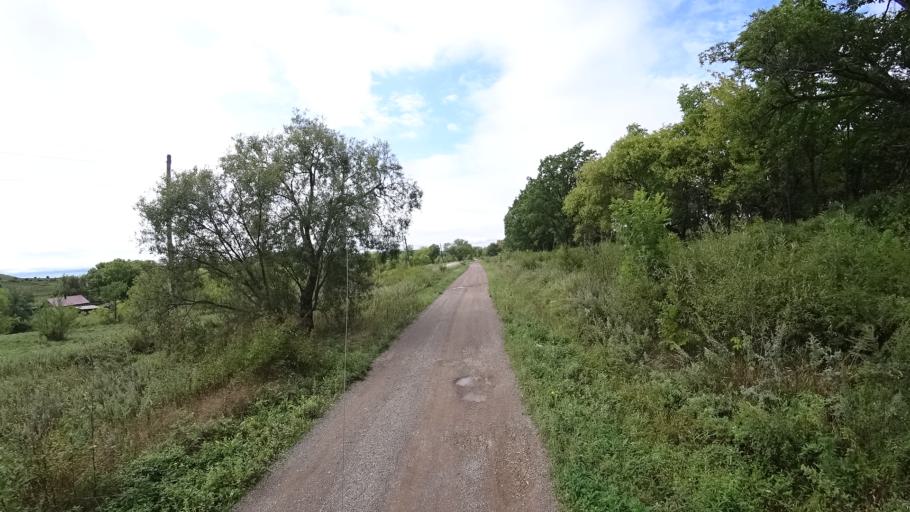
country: RU
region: Primorskiy
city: Lyalichi
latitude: 44.1396
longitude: 132.3851
